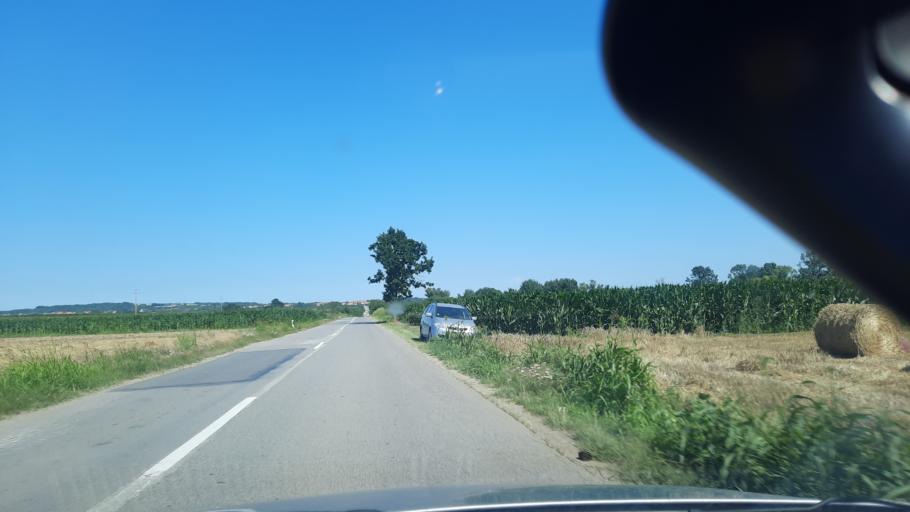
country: RS
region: Central Serbia
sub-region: Branicevski Okrug
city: Malo Crnice
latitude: 44.5773
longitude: 21.3366
